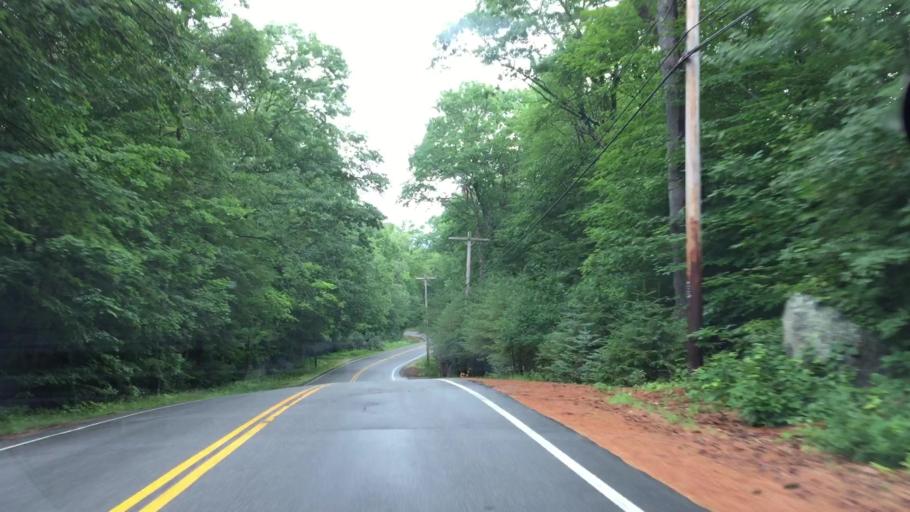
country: US
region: New Hampshire
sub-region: Carroll County
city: Center Harbor
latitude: 43.7363
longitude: -71.4771
